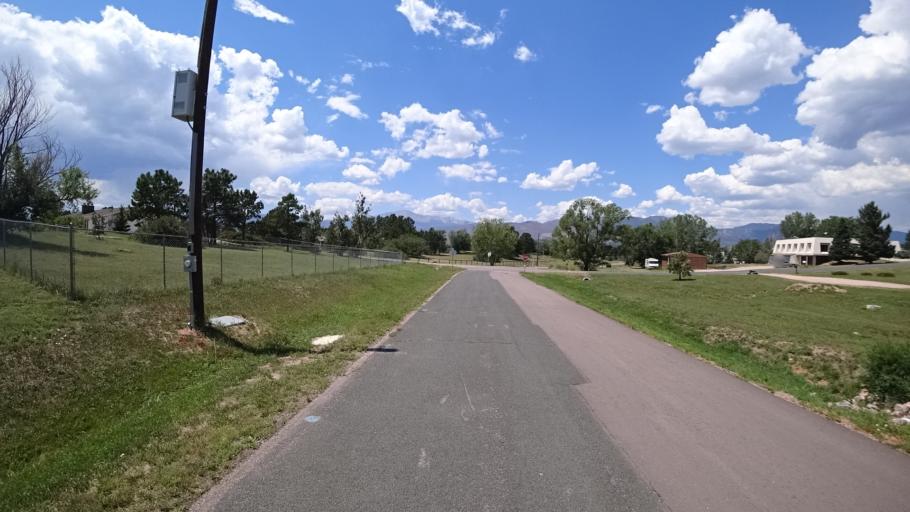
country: US
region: Colorado
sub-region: El Paso County
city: Air Force Academy
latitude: 38.9367
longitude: -104.8025
